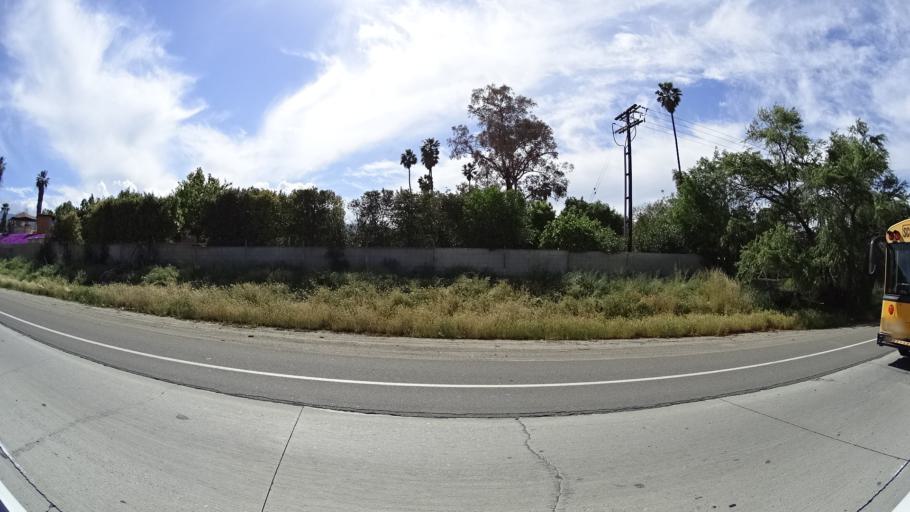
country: US
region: California
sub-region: Riverside County
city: El Cerrito
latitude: 33.8388
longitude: -117.5340
